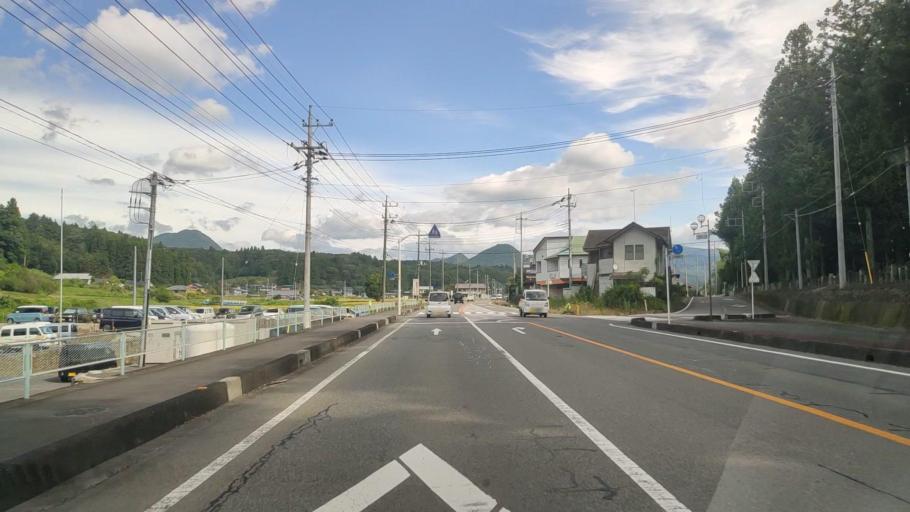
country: JP
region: Gunma
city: Nakanojomachi
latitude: 36.5926
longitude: 138.8615
